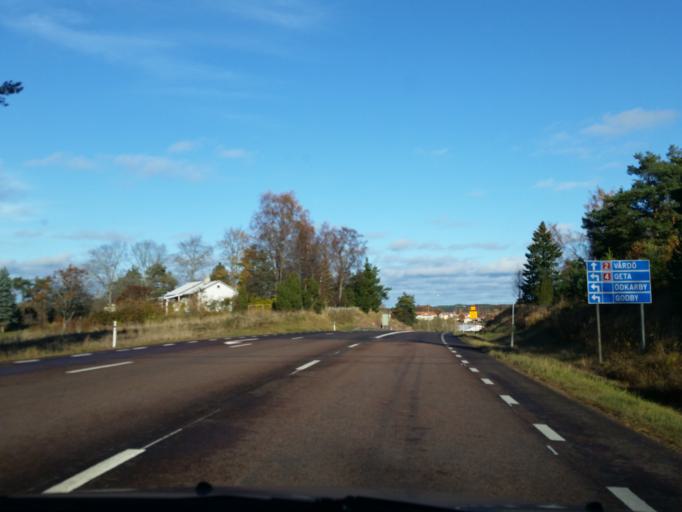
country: AX
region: Alands landsbygd
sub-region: Finstroem
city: Finstroem
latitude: 60.2260
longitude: 19.9859
